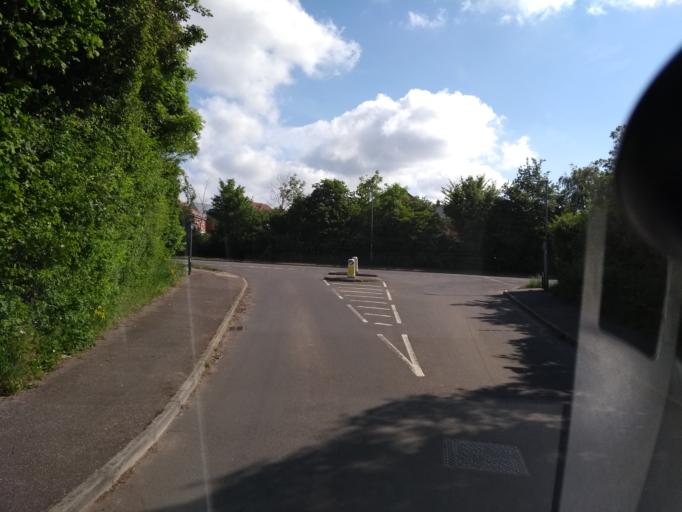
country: GB
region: England
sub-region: Somerset
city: Taunton
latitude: 51.0338
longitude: -3.0838
